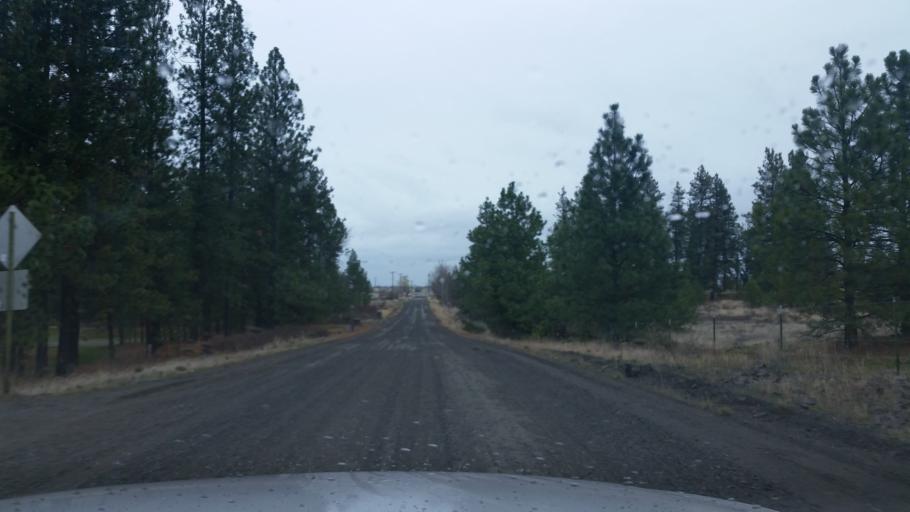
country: US
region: Washington
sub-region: Spokane County
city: Fairchild Air Force Base
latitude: 47.5826
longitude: -117.6288
